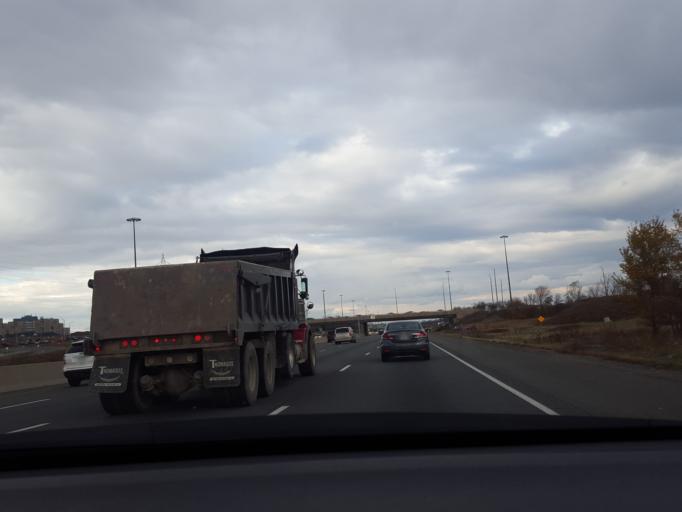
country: CA
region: Ontario
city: Mississauga
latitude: 43.5988
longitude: -79.6465
